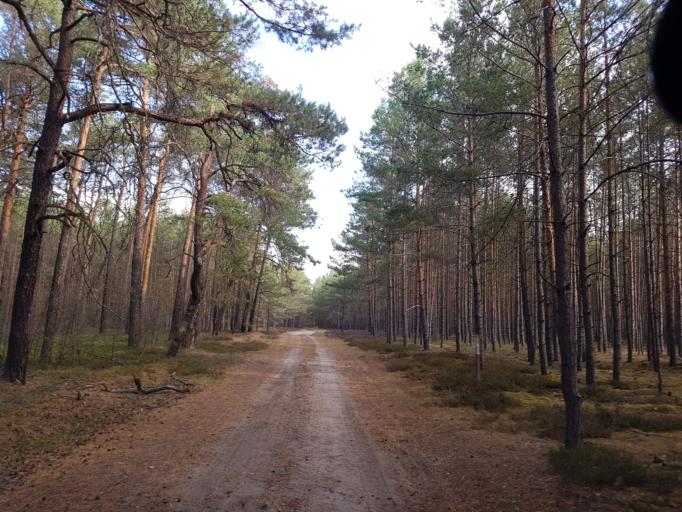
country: DE
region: Brandenburg
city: Finsterwalde
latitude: 51.5970
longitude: 13.7590
